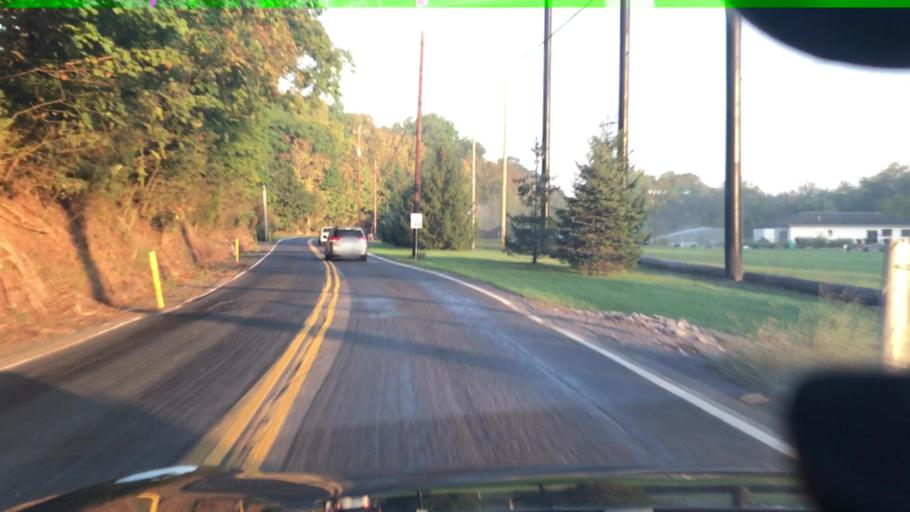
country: US
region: Pennsylvania
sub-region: Cumberland County
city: Lower Allen
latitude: 40.1745
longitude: -76.9222
